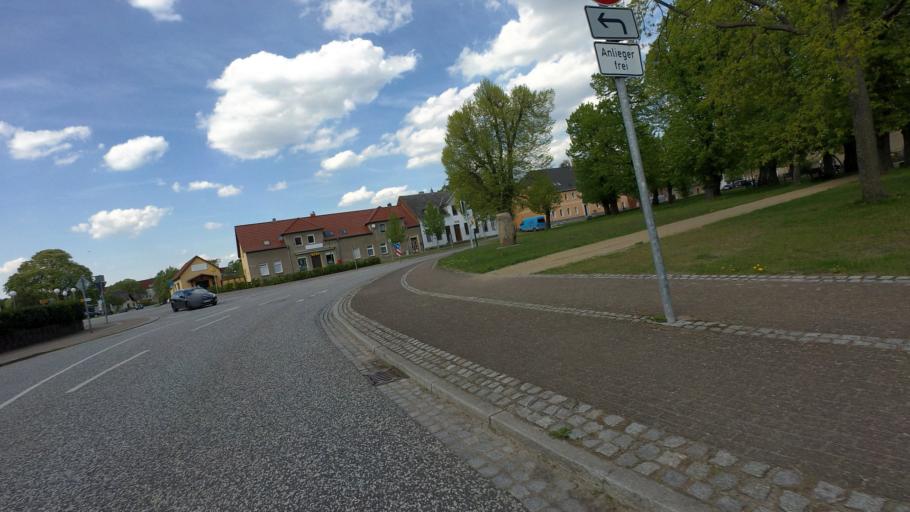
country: DE
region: Brandenburg
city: Marienwerder
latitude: 52.9066
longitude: 13.5318
